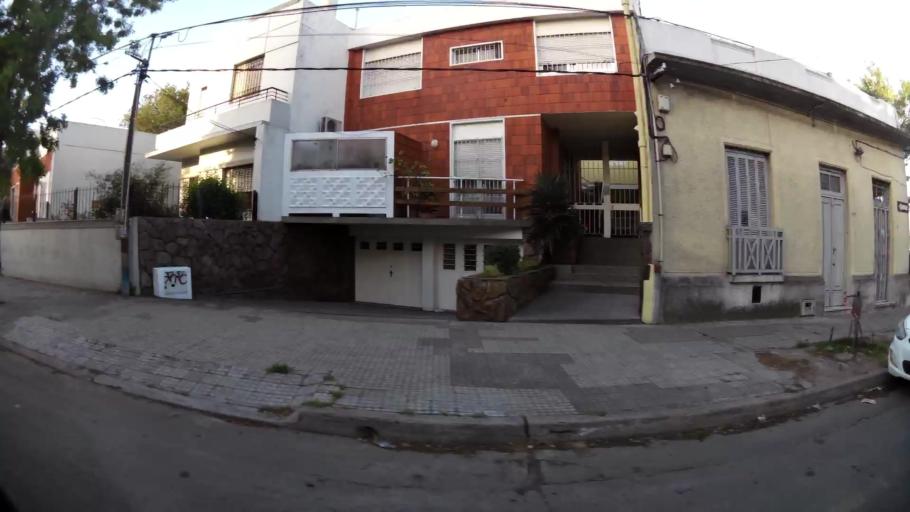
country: UY
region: Montevideo
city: Montevideo
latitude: -34.8860
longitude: -56.1466
